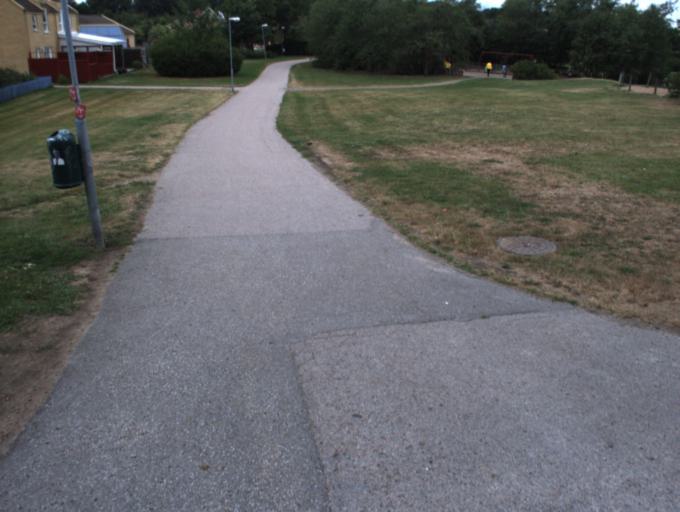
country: SE
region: Skane
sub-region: Helsingborg
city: Helsingborg
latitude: 56.0334
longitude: 12.7505
